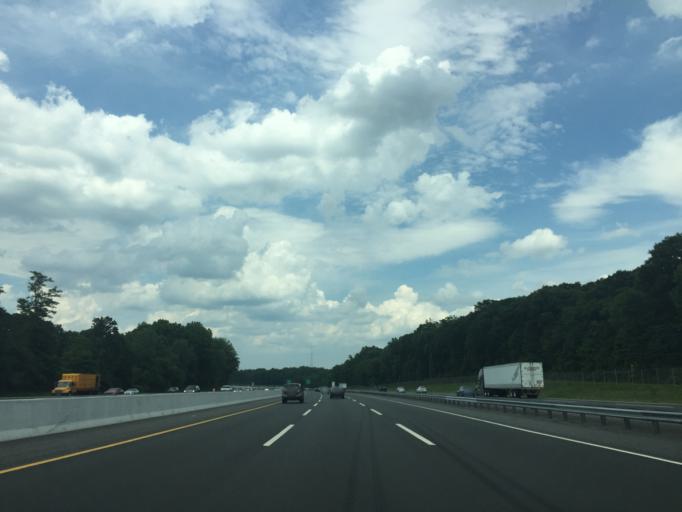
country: US
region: New Jersey
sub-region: Mercer County
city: Hightstown
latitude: 40.2423
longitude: -74.5261
